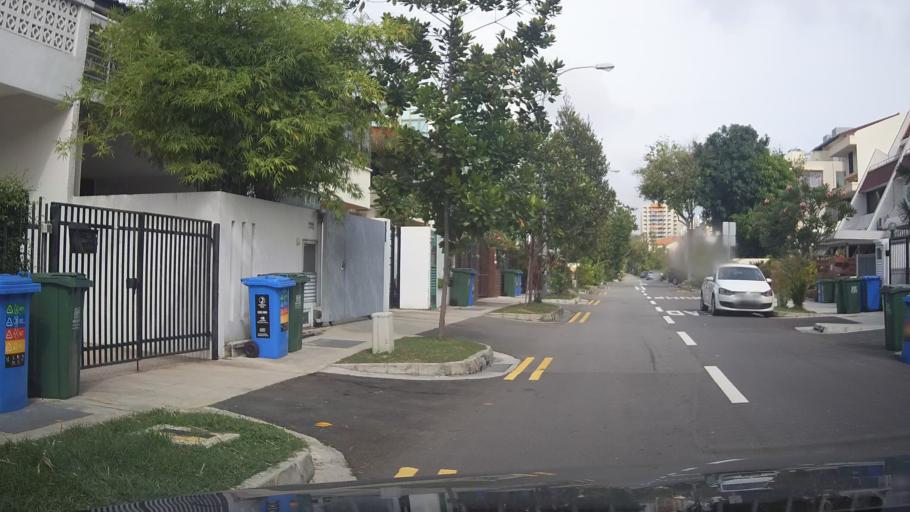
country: SG
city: Singapore
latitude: 1.3101
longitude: 103.9003
